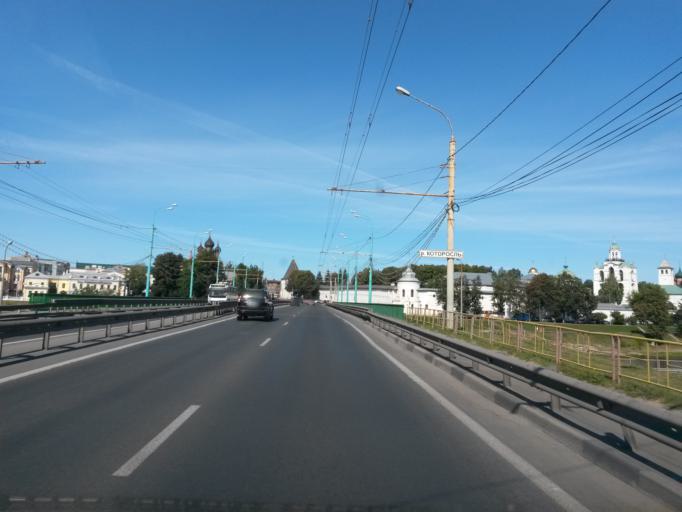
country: RU
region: Jaroslavl
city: Yaroslavl
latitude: 57.6190
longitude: 39.8861
